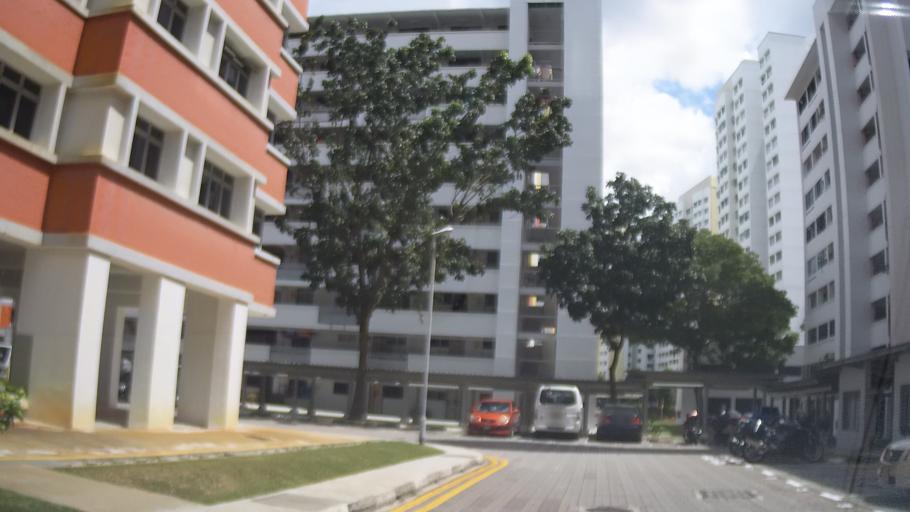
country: SG
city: Singapore
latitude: 1.3299
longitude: 103.8870
